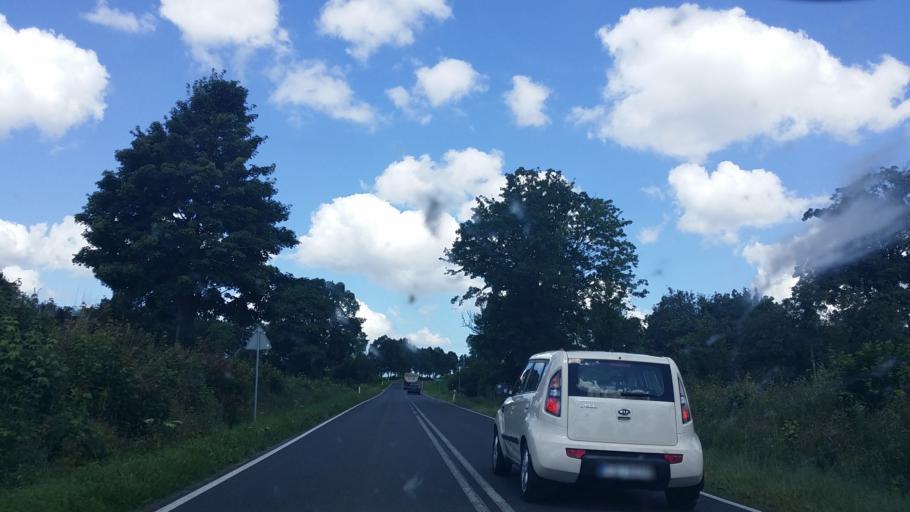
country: PL
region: West Pomeranian Voivodeship
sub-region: Powiat kolobrzeski
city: Goscino
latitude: 54.0123
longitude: 15.6625
